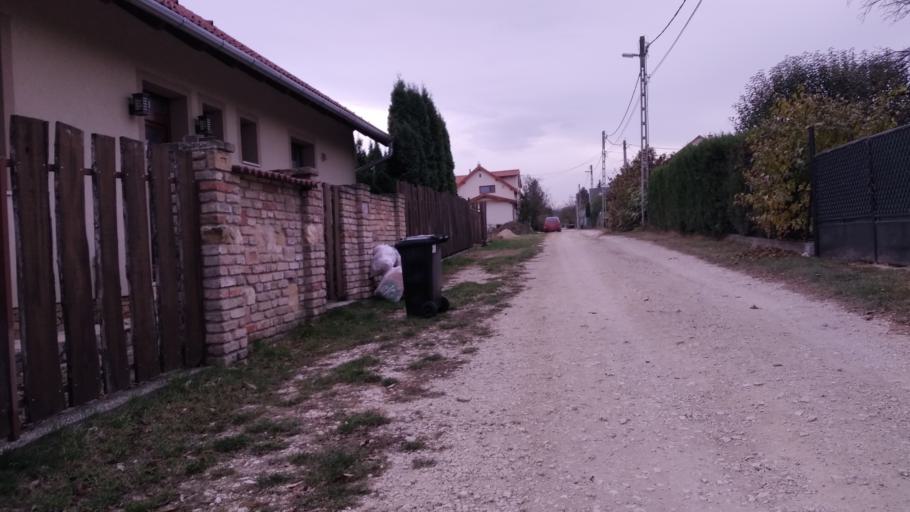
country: HU
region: Pest
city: Budakalasz
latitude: 47.6297
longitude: 19.0403
